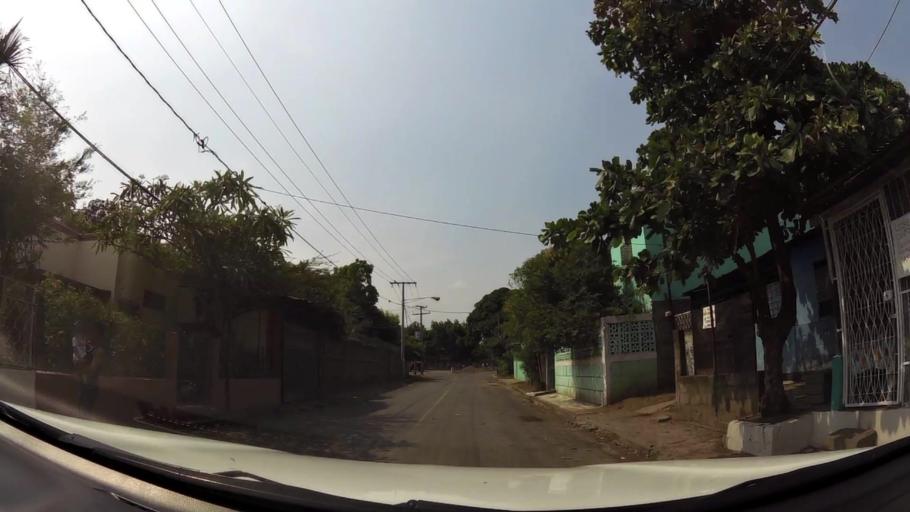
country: NI
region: Managua
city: Ciudad Sandino
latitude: 12.1300
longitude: -86.3137
